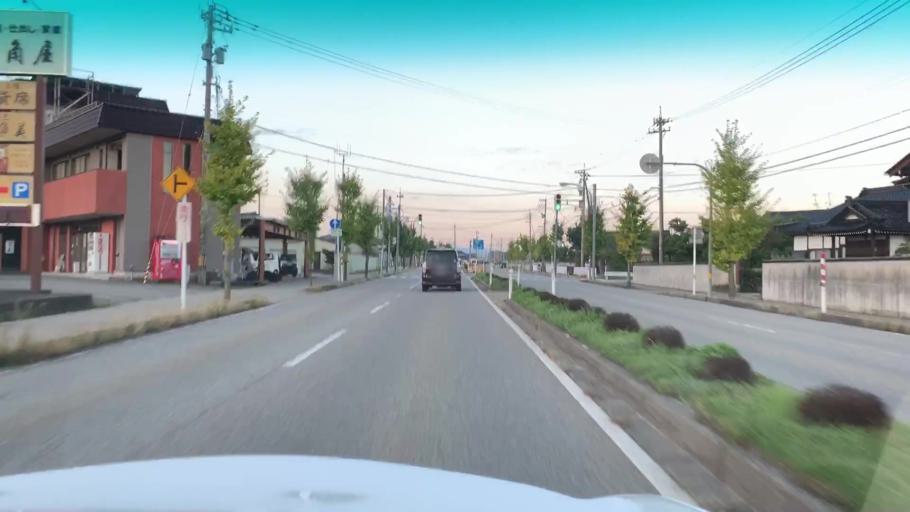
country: JP
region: Toyama
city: Kamiichi
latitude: 36.6876
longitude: 137.3369
